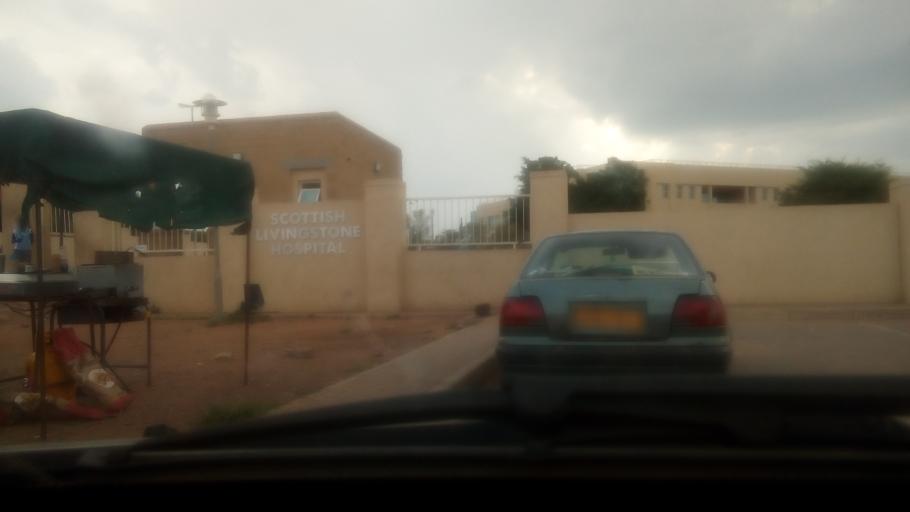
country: BW
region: Kweneng
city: Molepolole
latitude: -24.4115
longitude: 25.4882
